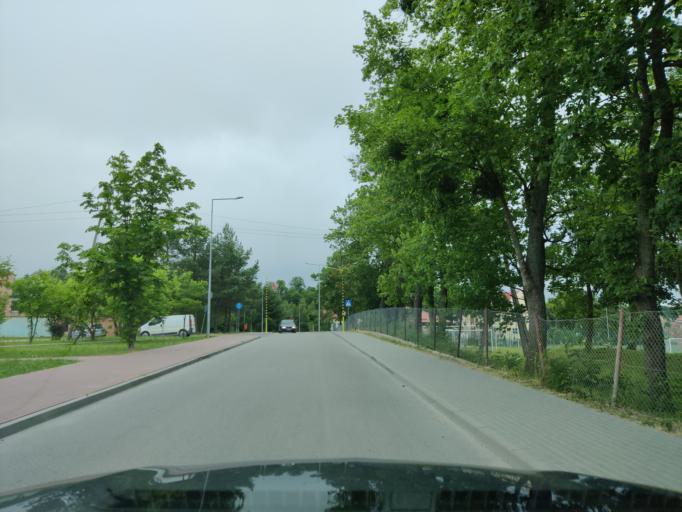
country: PL
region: Warmian-Masurian Voivodeship
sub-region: Powiat gizycki
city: Ryn
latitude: 53.9353
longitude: 21.5386
